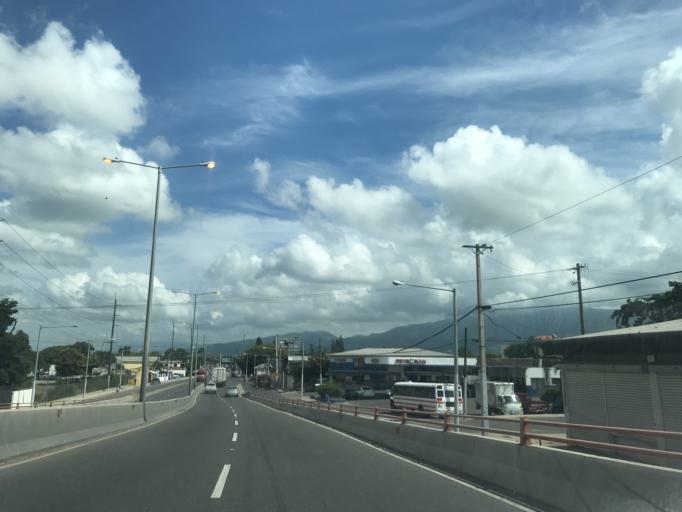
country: DO
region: Santiago
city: Santiago de los Caballeros
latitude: 19.4874
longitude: -70.7328
